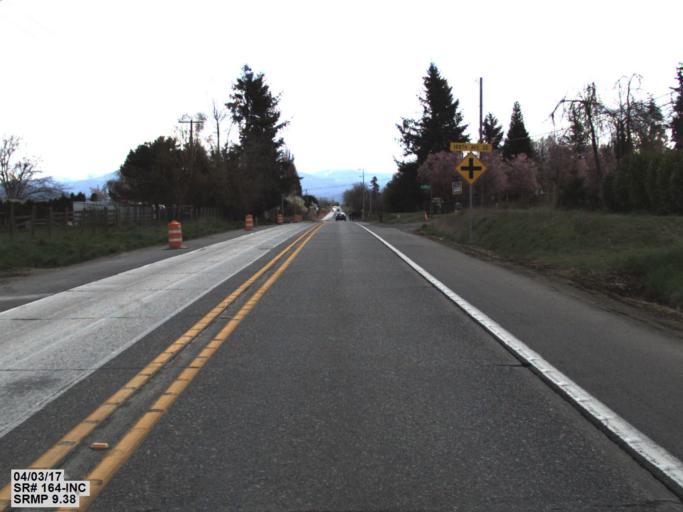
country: US
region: Washington
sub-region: Pierce County
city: Buckley
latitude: 47.2196
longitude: -122.0926
